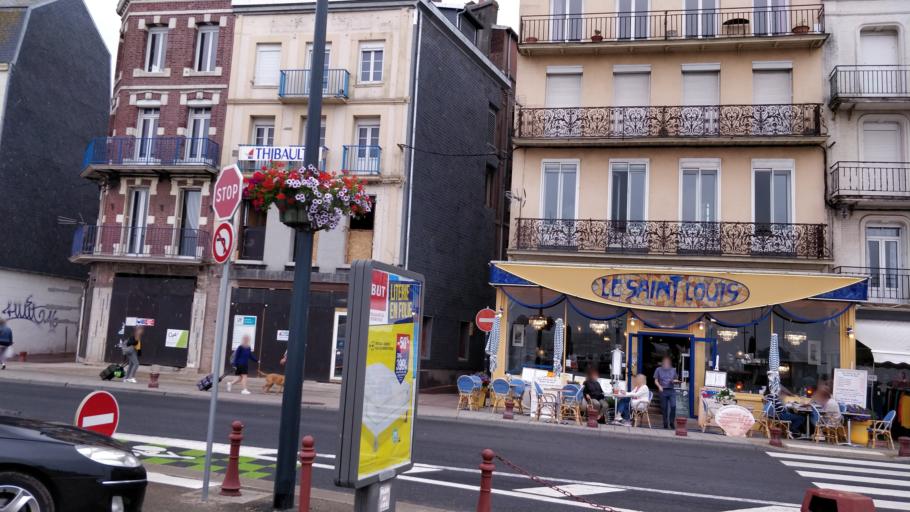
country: FR
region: Haute-Normandie
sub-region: Departement de la Seine-Maritime
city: Le Treport
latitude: 50.0617
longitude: 1.3711
